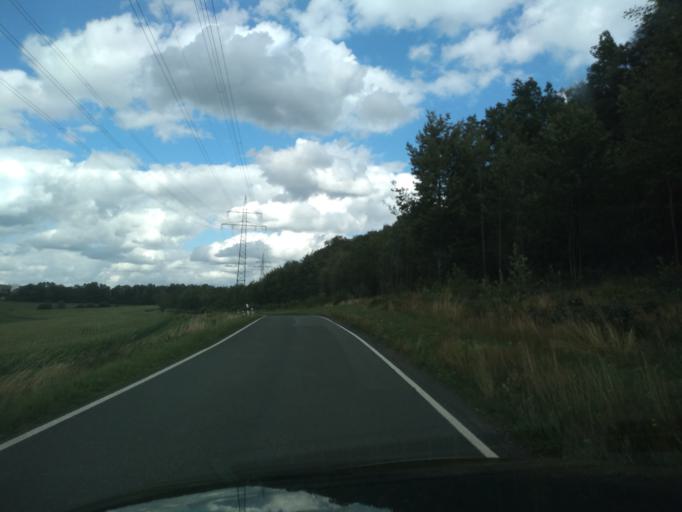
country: DE
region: North Rhine-Westphalia
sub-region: Regierungsbezirk Arnsberg
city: Luedenscheid
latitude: 51.2357
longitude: 7.6000
